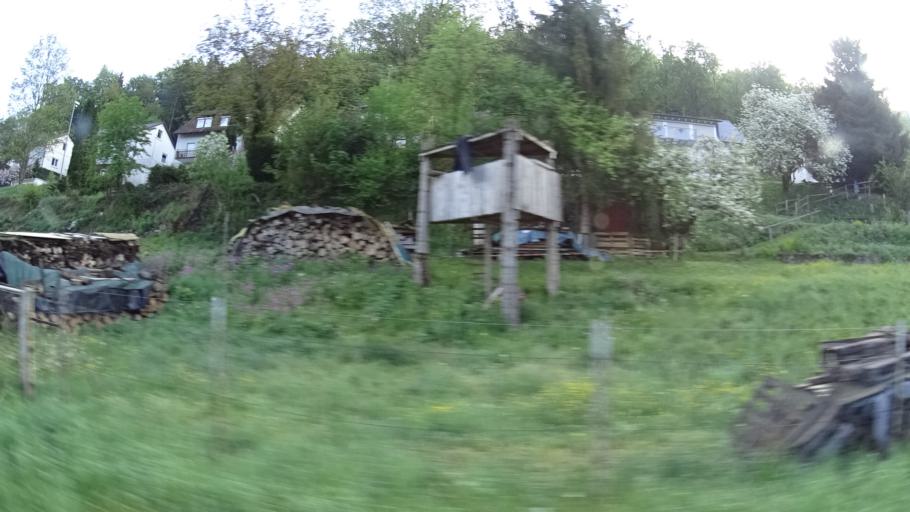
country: DE
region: Baden-Wuerttemberg
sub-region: Karlsruhe Region
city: Empfingen
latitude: 48.4159
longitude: 8.7638
